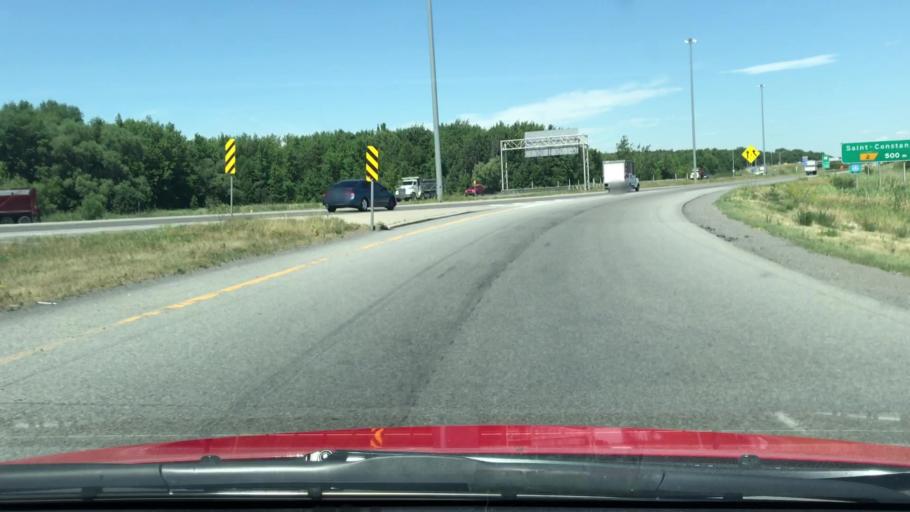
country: CA
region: Quebec
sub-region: Monteregie
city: Saint-Constant
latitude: 45.3718
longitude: -73.6223
